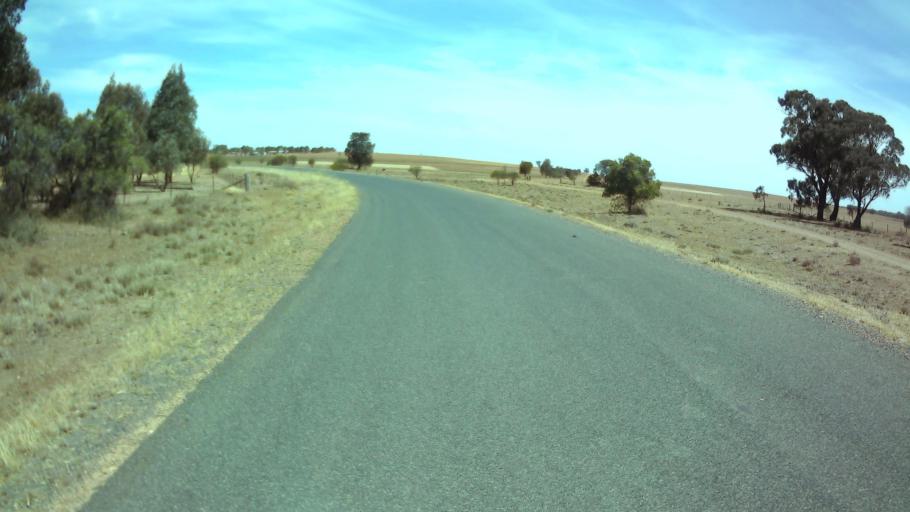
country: AU
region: New South Wales
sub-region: Weddin
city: Grenfell
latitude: -33.8878
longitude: 147.7415
